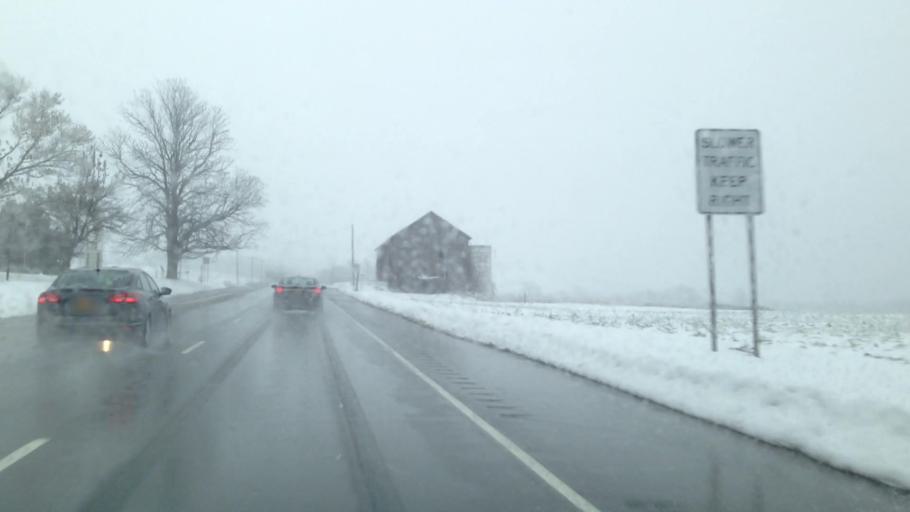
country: US
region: New York
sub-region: Onondaga County
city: Peru
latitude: 43.0369
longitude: -76.3941
